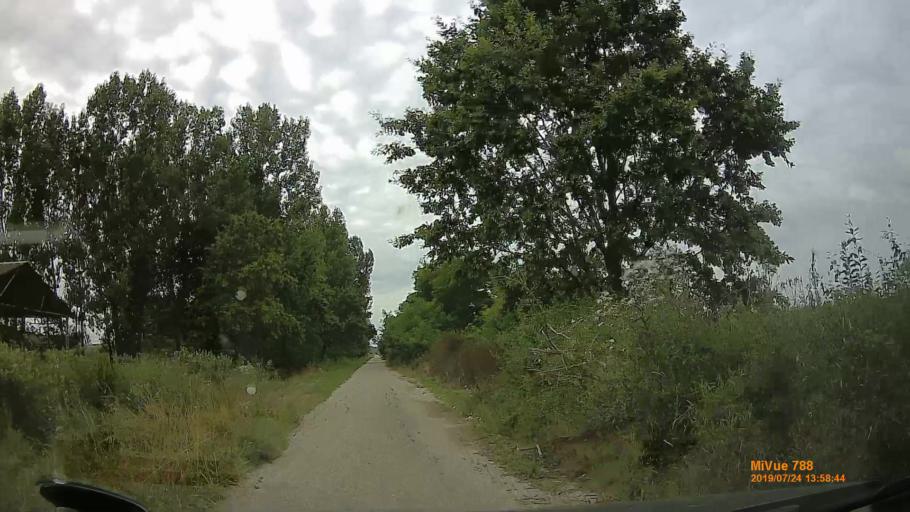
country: HU
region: Szabolcs-Szatmar-Bereg
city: Aranyosapati
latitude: 48.2586
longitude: 22.3209
